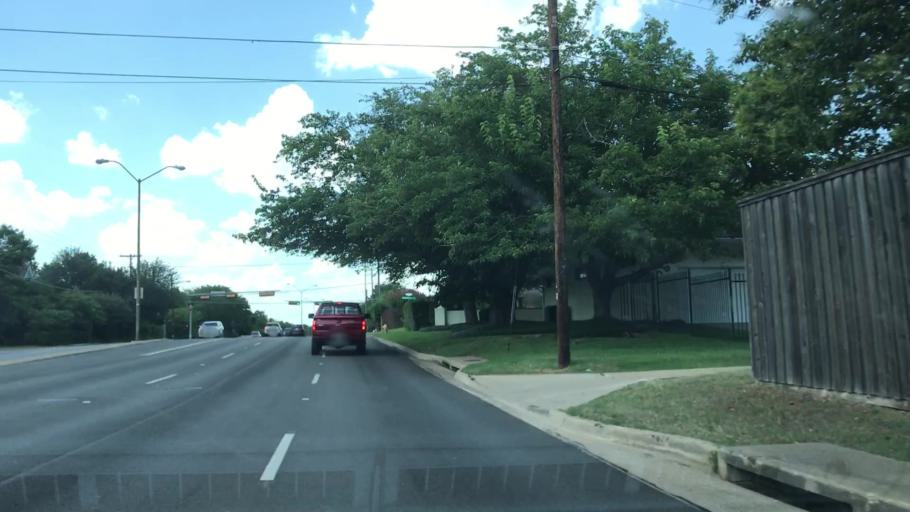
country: US
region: Texas
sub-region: Dallas County
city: Addison
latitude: 32.9084
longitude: -96.8382
